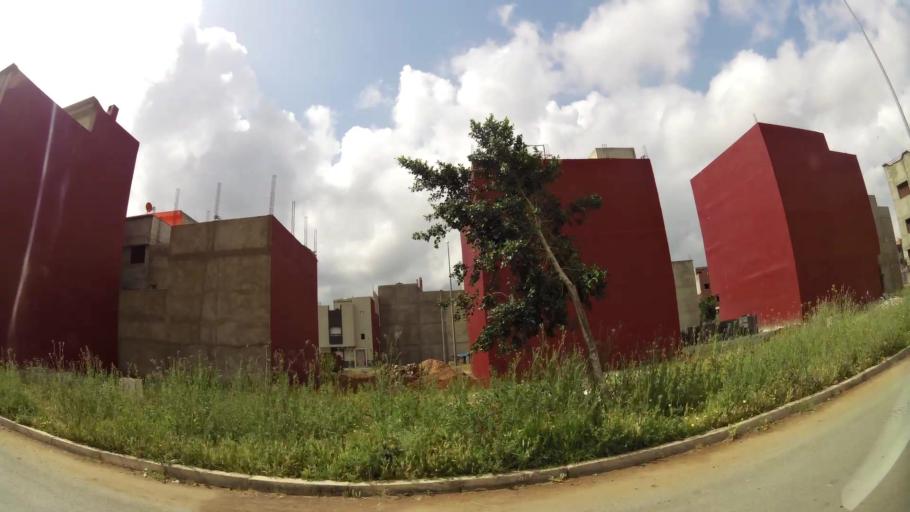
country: MA
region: Rabat-Sale-Zemmour-Zaer
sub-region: Khemisset
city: Tiflet
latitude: 33.8984
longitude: -6.3344
